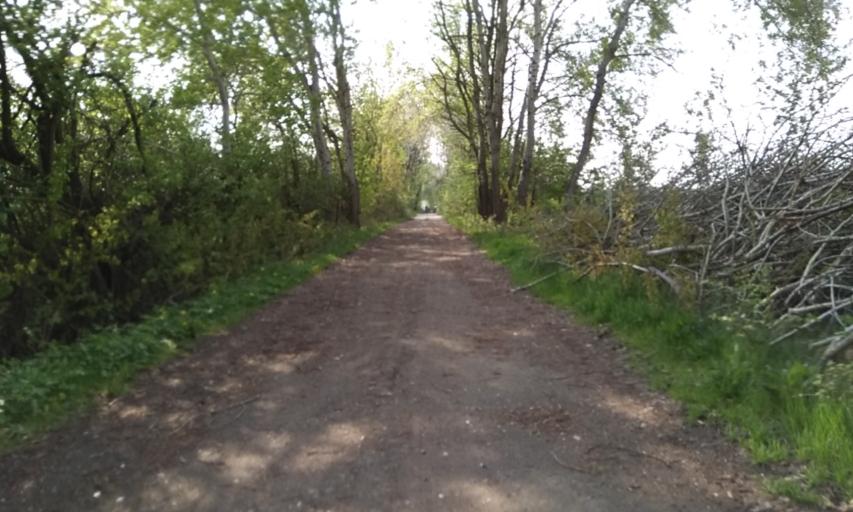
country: DE
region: Lower Saxony
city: Apensen
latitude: 53.4376
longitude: 9.5780
